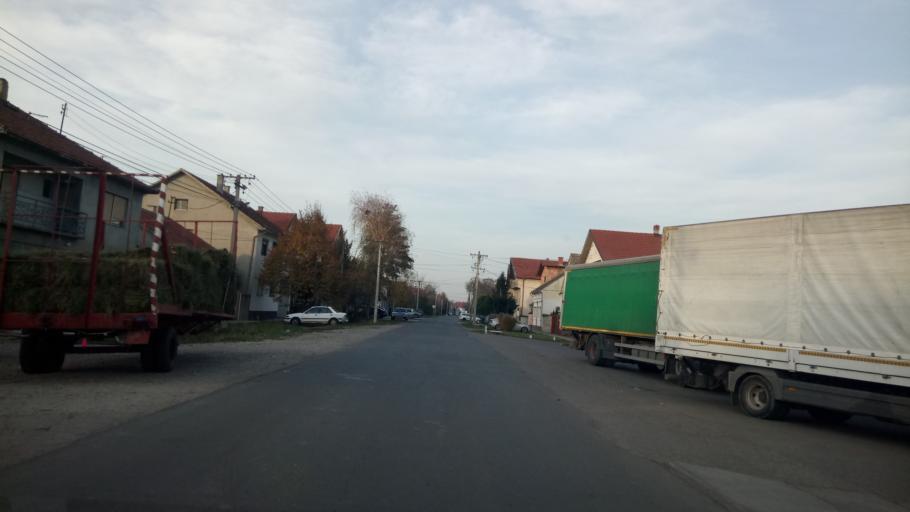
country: RS
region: Autonomna Pokrajina Vojvodina
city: Nova Pazova
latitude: 44.9376
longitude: 20.2153
